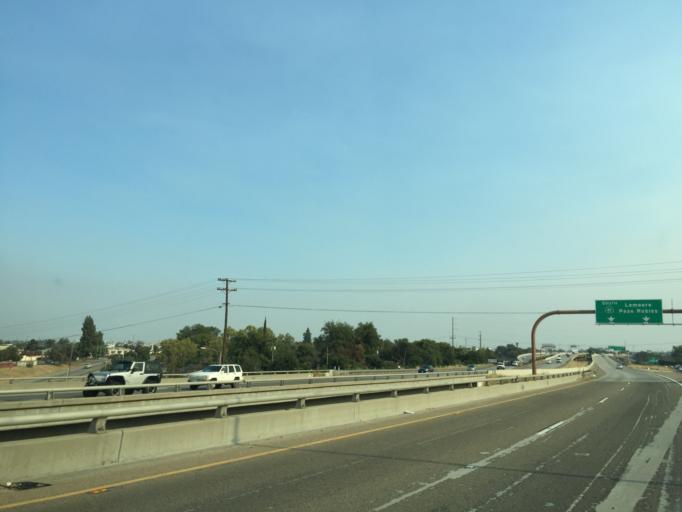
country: US
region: California
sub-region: Fresno County
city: Fresno
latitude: 36.7219
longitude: -119.7855
